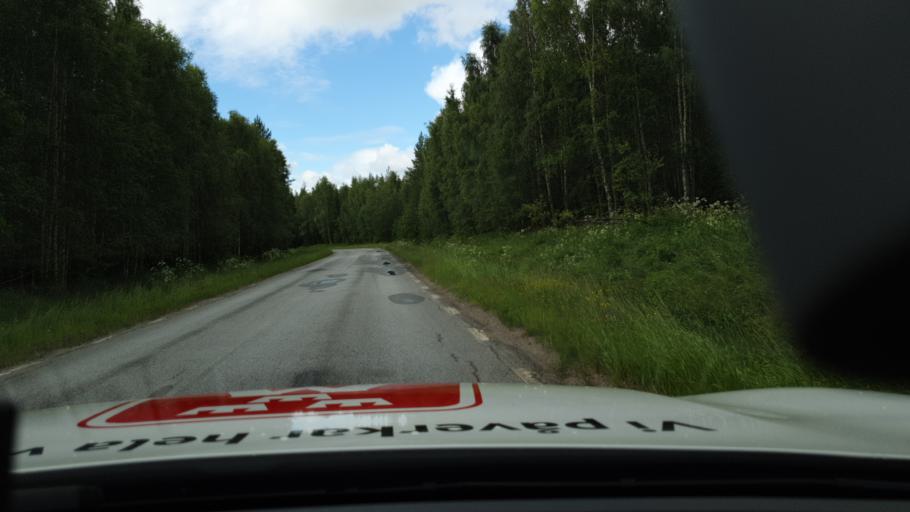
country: SE
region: Norrbotten
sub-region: Lulea Kommun
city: Sodra Sunderbyn
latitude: 65.4619
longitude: 21.9084
